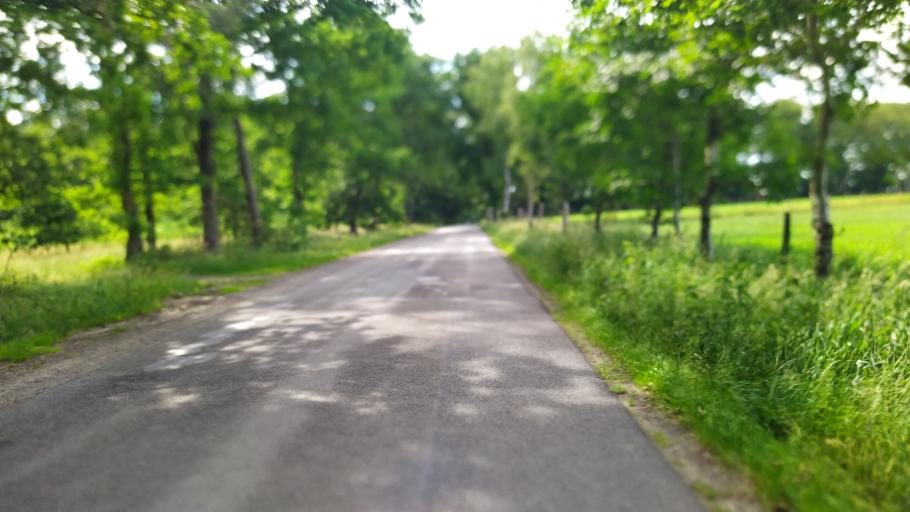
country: DE
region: Lower Saxony
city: Armstorf
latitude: 53.6074
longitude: 9.0437
